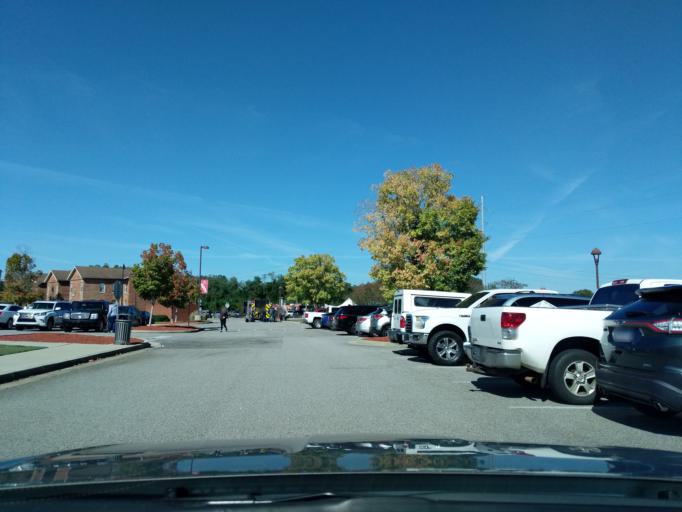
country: US
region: Georgia
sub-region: Richmond County
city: Augusta
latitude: 33.4863
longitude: -81.9942
